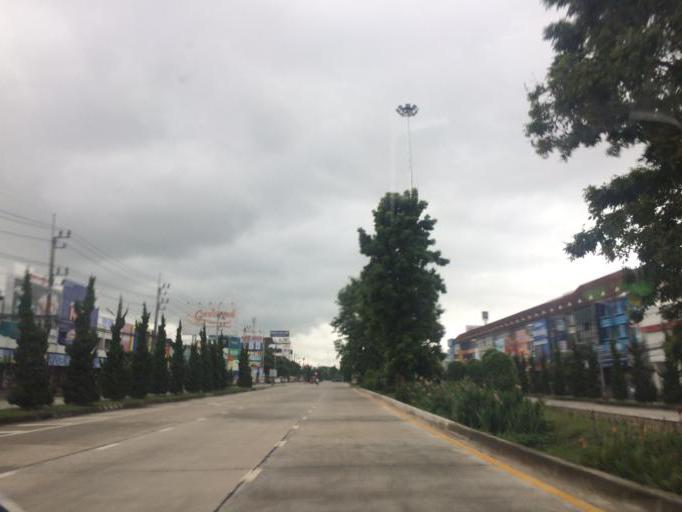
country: TH
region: Chiang Rai
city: Chiang Rai
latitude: 19.9000
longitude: 99.8395
